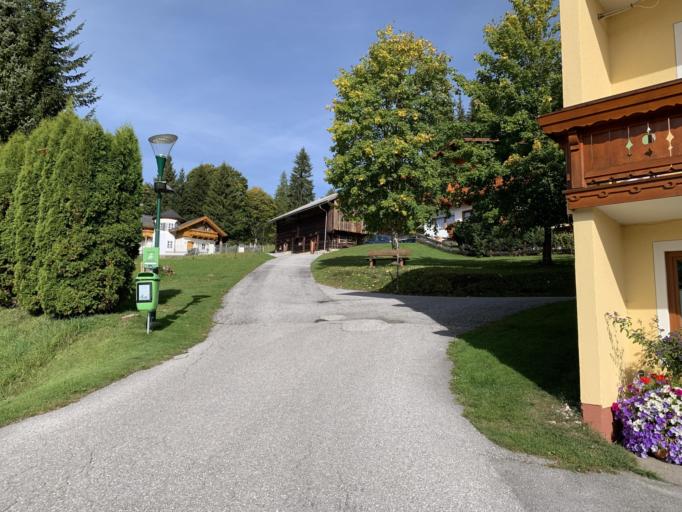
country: AT
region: Styria
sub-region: Politischer Bezirk Liezen
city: Schladming
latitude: 47.4304
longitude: 13.6448
